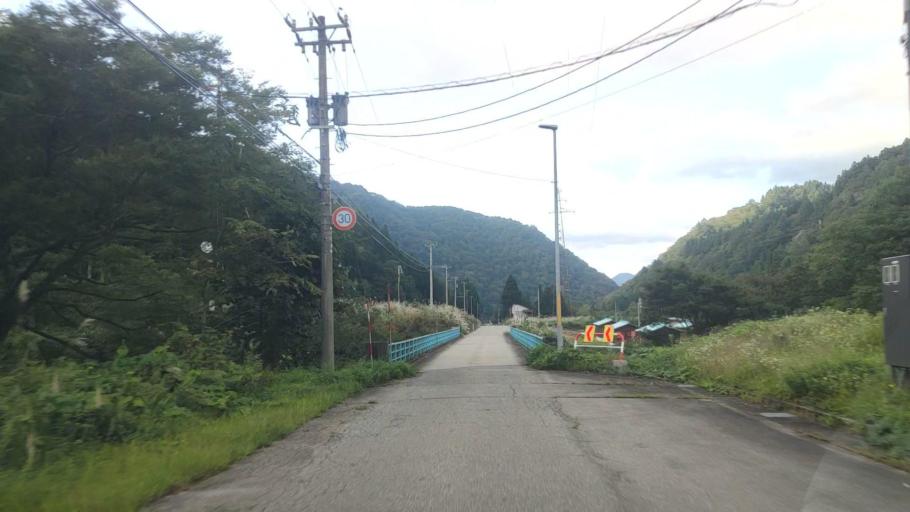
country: JP
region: Toyama
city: Yatsuomachi-higashikumisaka
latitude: 36.4331
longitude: 137.0819
